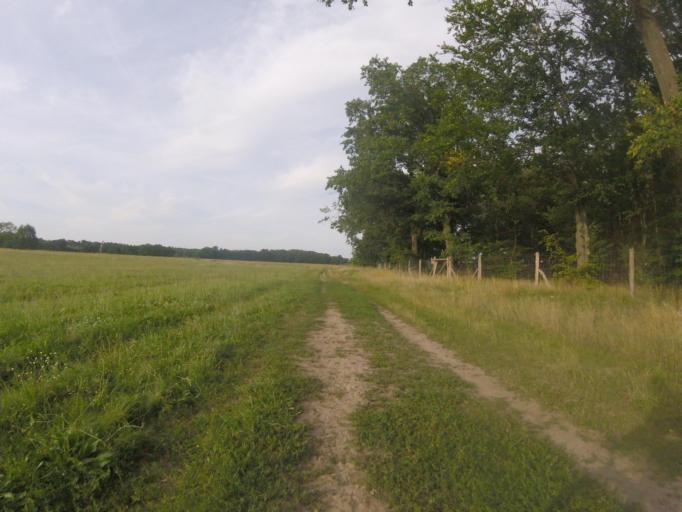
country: DE
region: Brandenburg
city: Schonefeld
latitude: 52.3527
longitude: 13.4583
